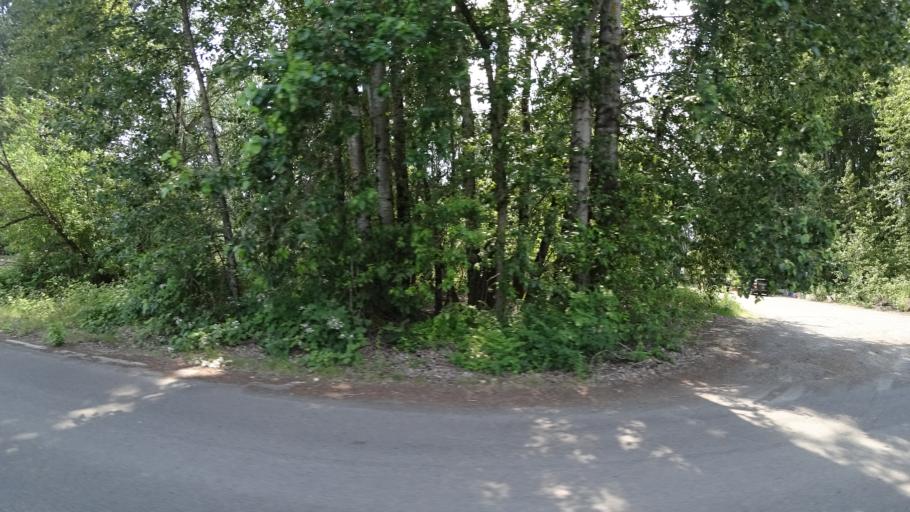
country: US
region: Washington
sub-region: Clark County
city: Lake Shore
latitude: 45.6404
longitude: -122.7622
